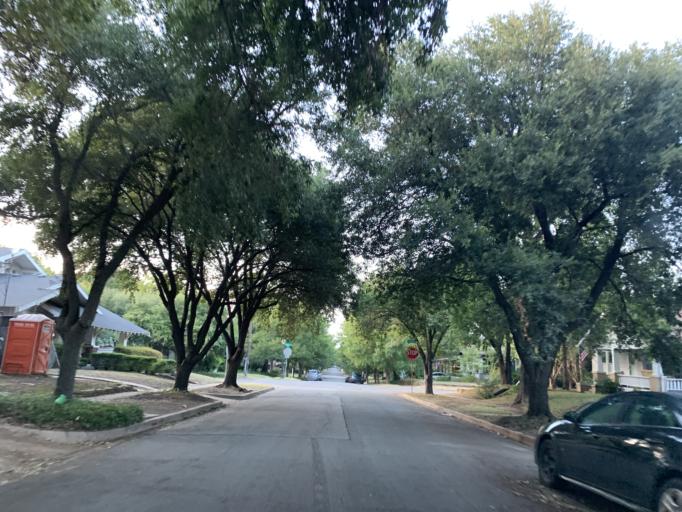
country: US
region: Texas
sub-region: Dallas County
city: Cockrell Hill
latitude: 32.7447
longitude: -96.8404
